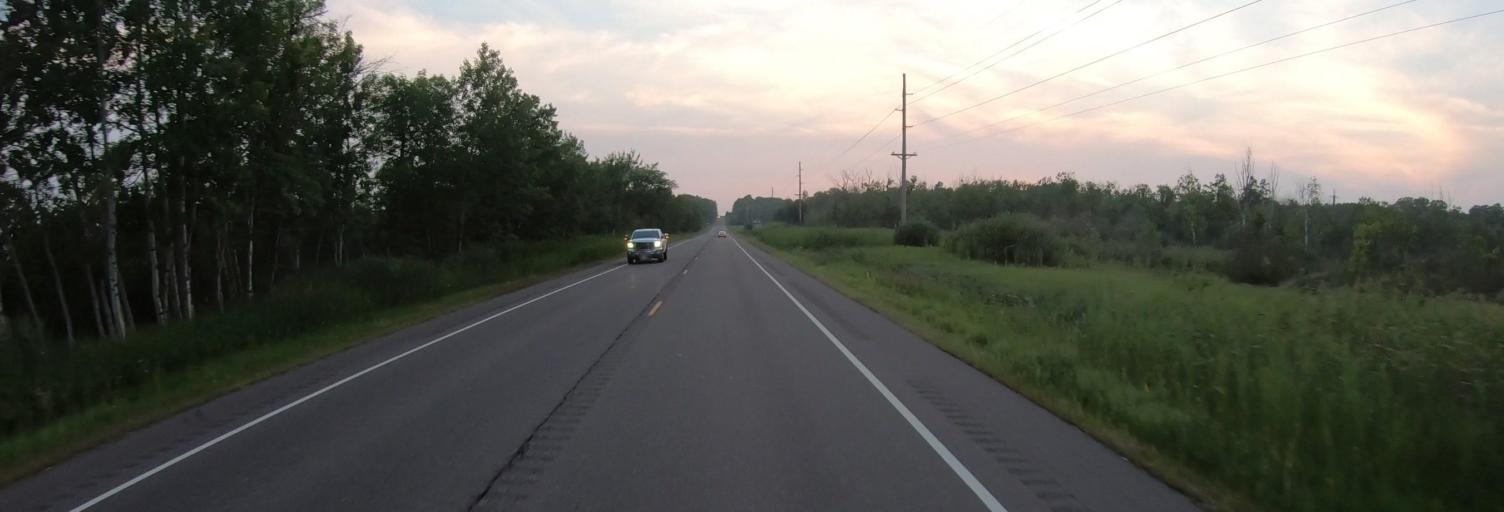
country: US
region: Minnesota
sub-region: Pine County
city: Rock Creek
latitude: 45.7735
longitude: -92.8373
